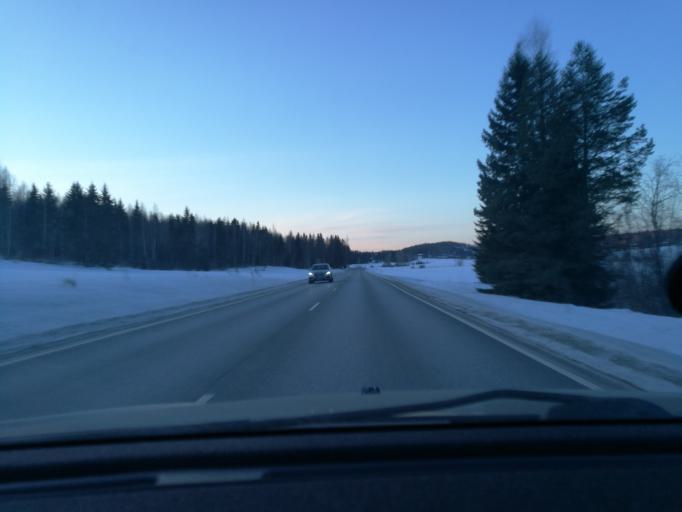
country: FI
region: Uusimaa
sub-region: Helsinki
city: Vihti
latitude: 60.4276
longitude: 24.4307
